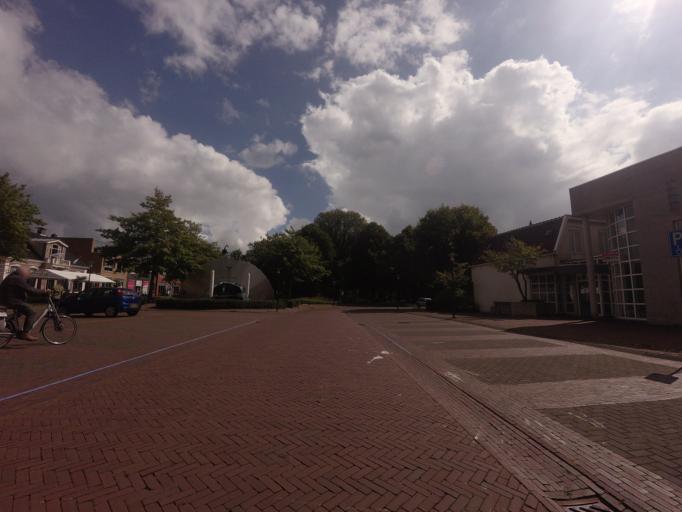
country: NL
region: Friesland
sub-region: Gemeente Skarsterlan
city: Joure
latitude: 52.9650
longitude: 5.7999
